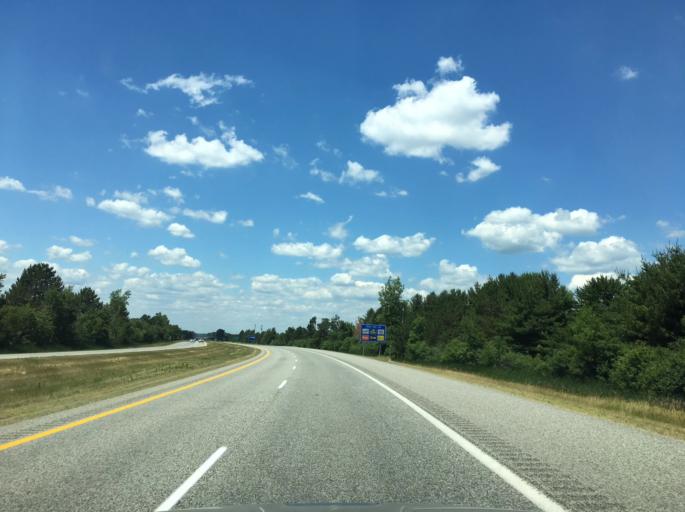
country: US
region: Michigan
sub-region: Midland County
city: Midland
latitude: 43.6557
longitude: -84.2110
